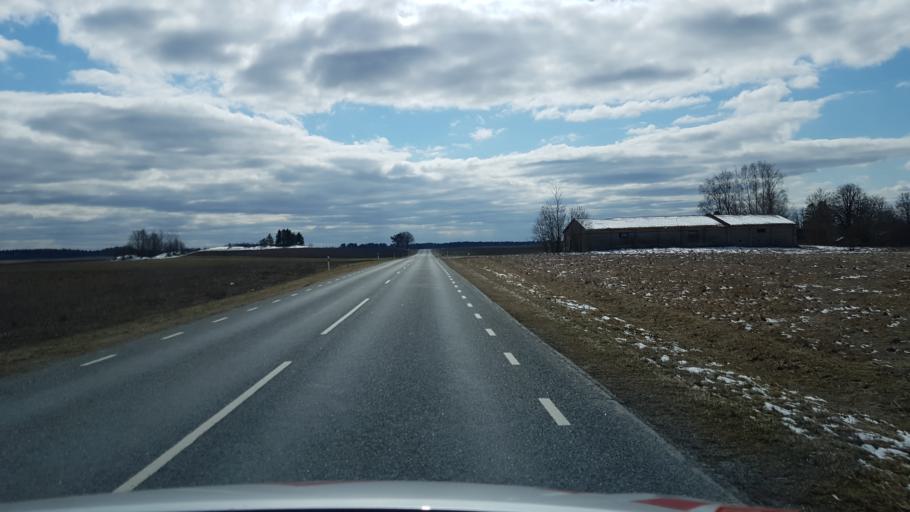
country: EE
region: Laeaene-Virumaa
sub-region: Tapa vald
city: Tapa
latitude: 59.3071
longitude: 26.0004
